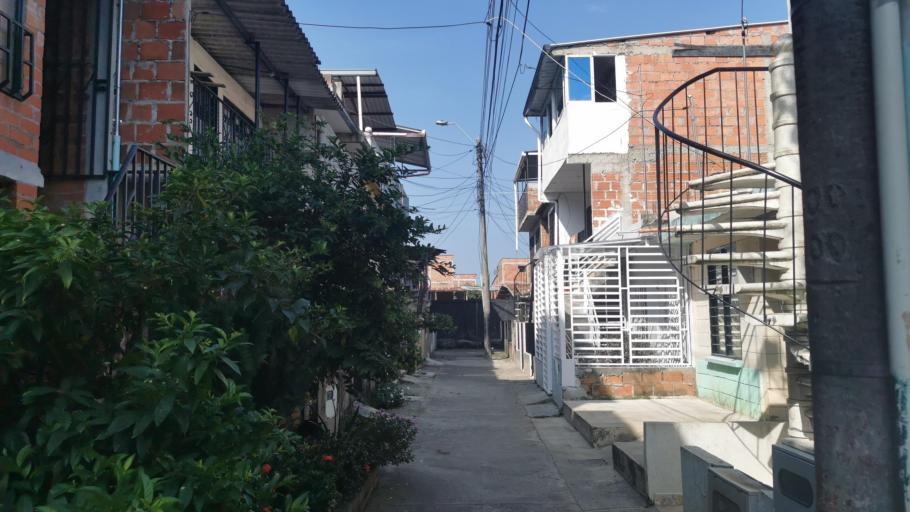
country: CO
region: Valle del Cauca
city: Jamundi
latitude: 3.2551
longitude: -76.5482
